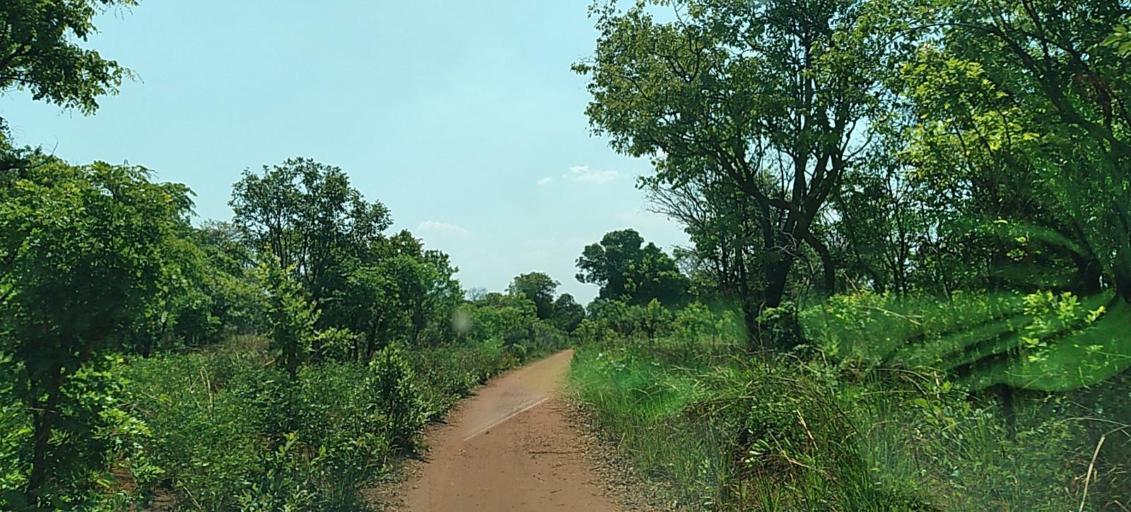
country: CD
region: Katanga
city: Kolwezi
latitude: -11.2814
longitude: 25.1378
